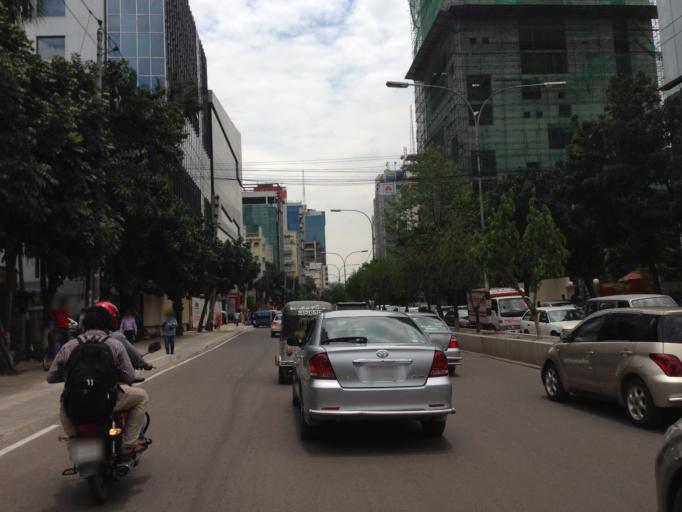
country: BD
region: Dhaka
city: Paltan
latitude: 23.7849
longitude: 90.4171
